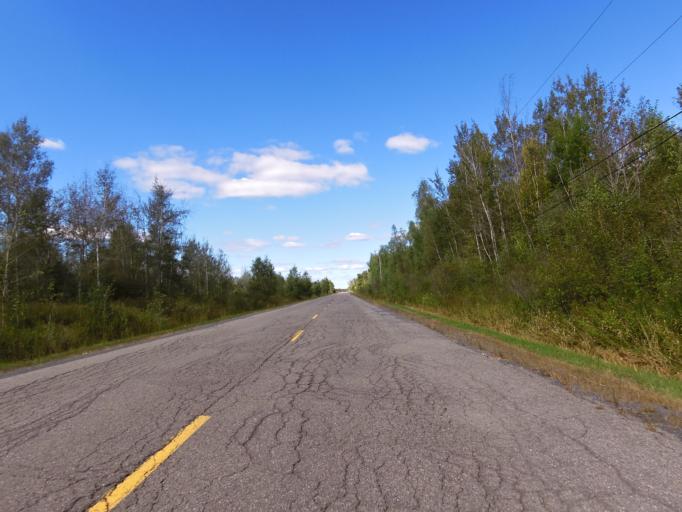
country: CA
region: Ontario
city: Ottawa
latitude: 45.3210
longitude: -75.4858
